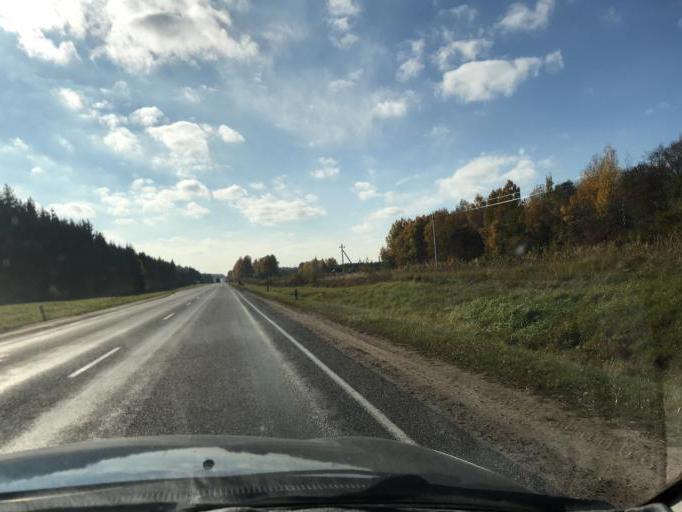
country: BY
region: Grodnenskaya
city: Voranava
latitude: 54.2116
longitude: 25.3517
